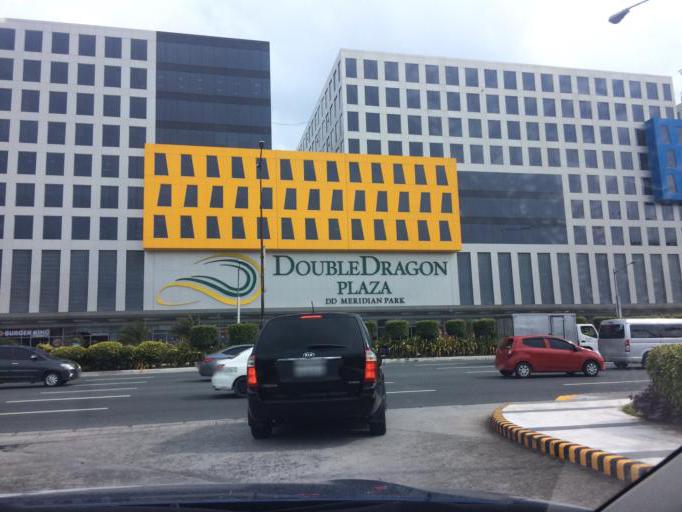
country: PH
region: Metro Manila
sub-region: Makati City
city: Makati City
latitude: 14.5369
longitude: 120.9903
